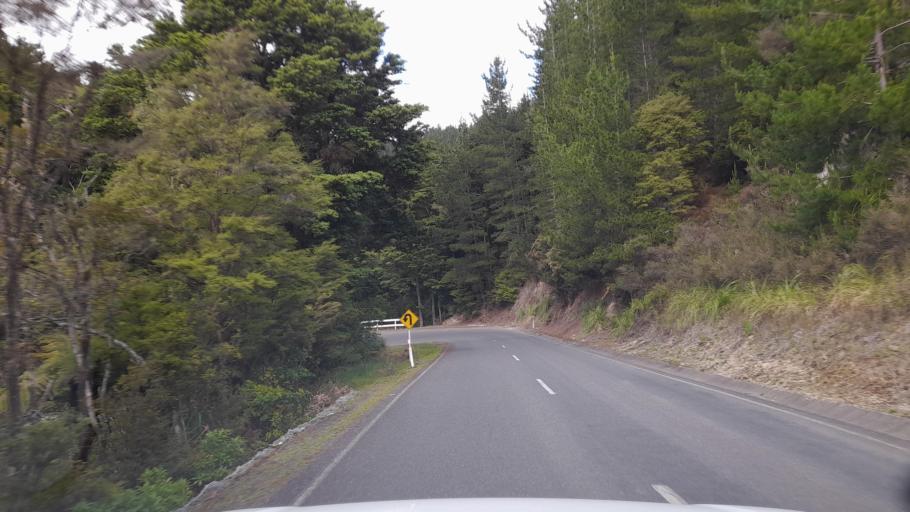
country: NZ
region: Northland
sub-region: Whangarei
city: Maungatapere
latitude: -35.6706
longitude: 174.0397
